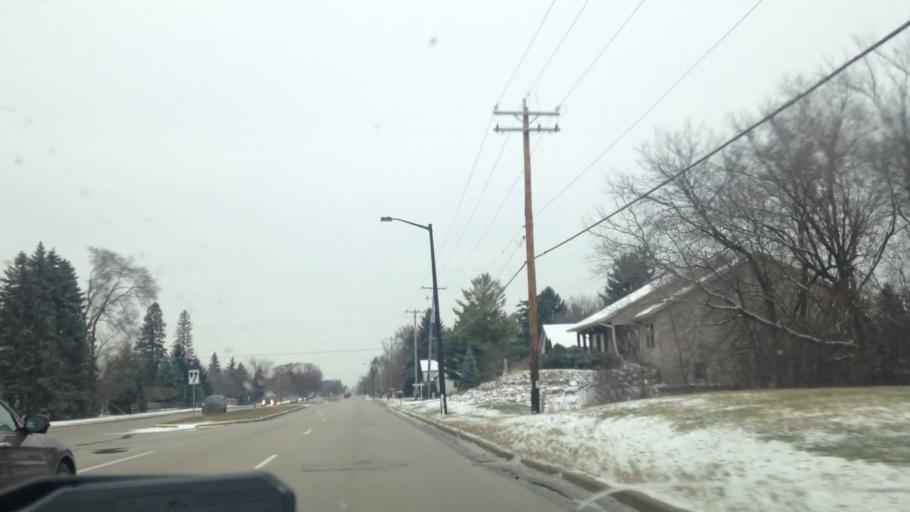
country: US
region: Wisconsin
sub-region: Waukesha County
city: Butler
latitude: 43.1109
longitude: -88.1054
